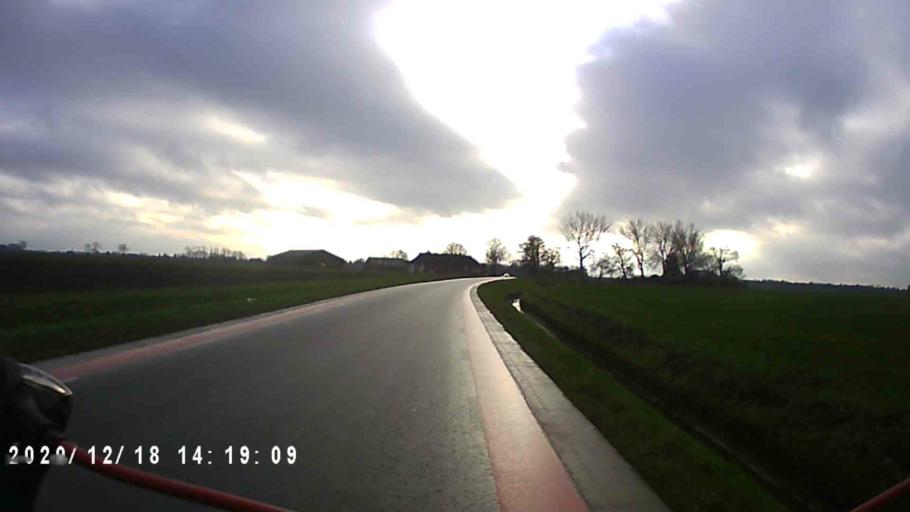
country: NL
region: Groningen
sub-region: Gemeente Bedum
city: Bedum
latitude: 53.2574
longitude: 6.6461
